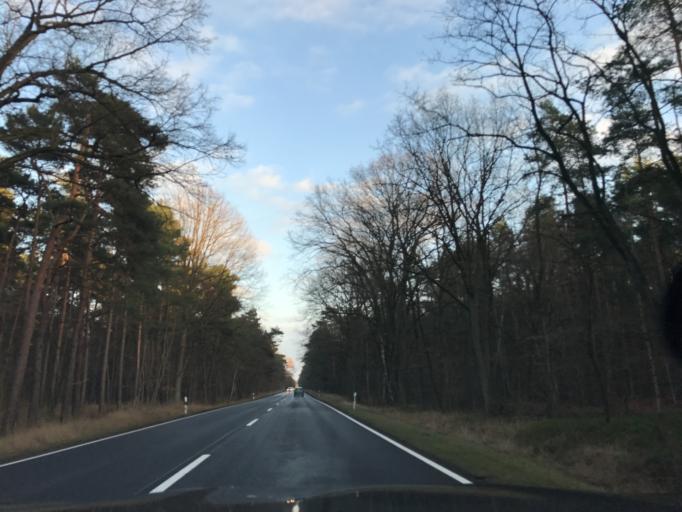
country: DE
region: Brandenburg
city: Bensdorf
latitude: 52.4113
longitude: 12.2785
